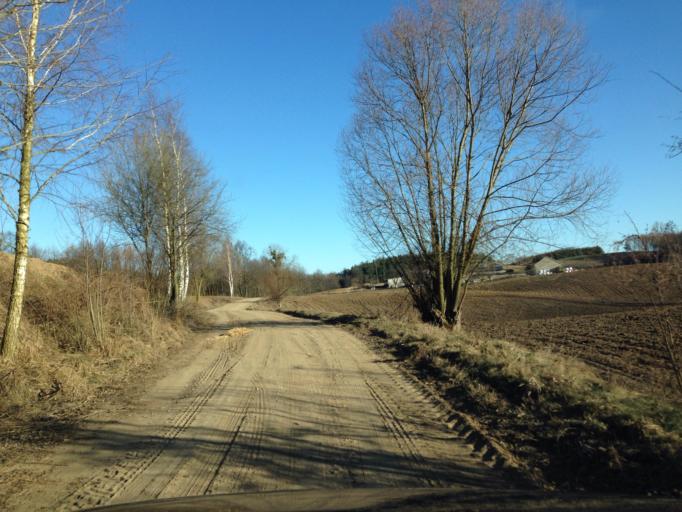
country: PL
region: Kujawsko-Pomorskie
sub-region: Powiat brodnicki
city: Brzozie
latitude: 53.3056
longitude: 19.6563
